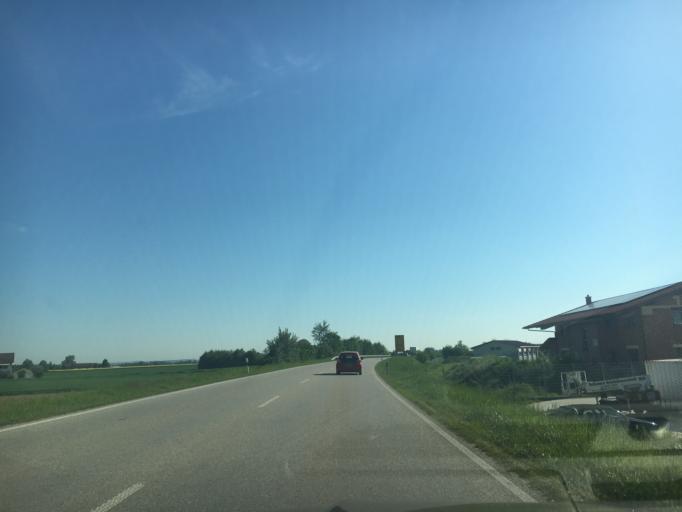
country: DE
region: Bavaria
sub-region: Upper Bavaria
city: Unterneukirchen
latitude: 48.1676
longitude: 12.6139
